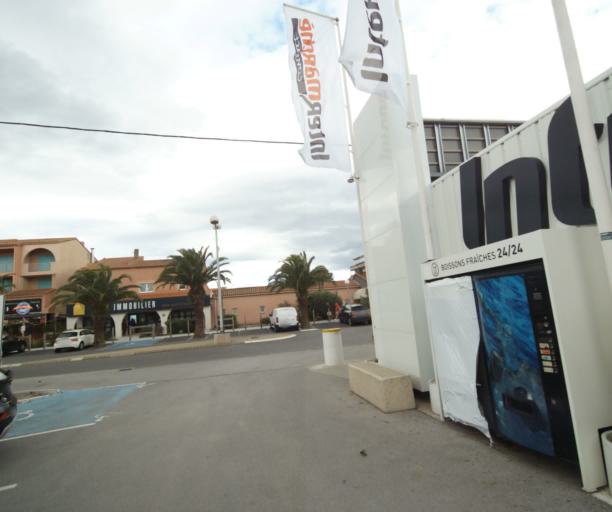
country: FR
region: Languedoc-Roussillon
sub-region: Departement des Pyrenees-Orientales
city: Argelers
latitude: 42.5548
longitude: 3.0430
